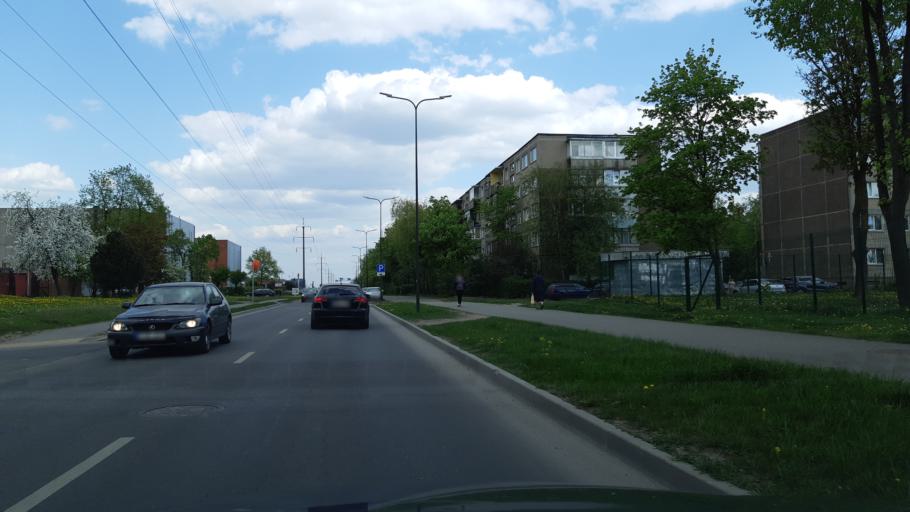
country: LT
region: Kauno apskritis
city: Dainava (Kaunas)
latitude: 54.9249
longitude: 23.9707
